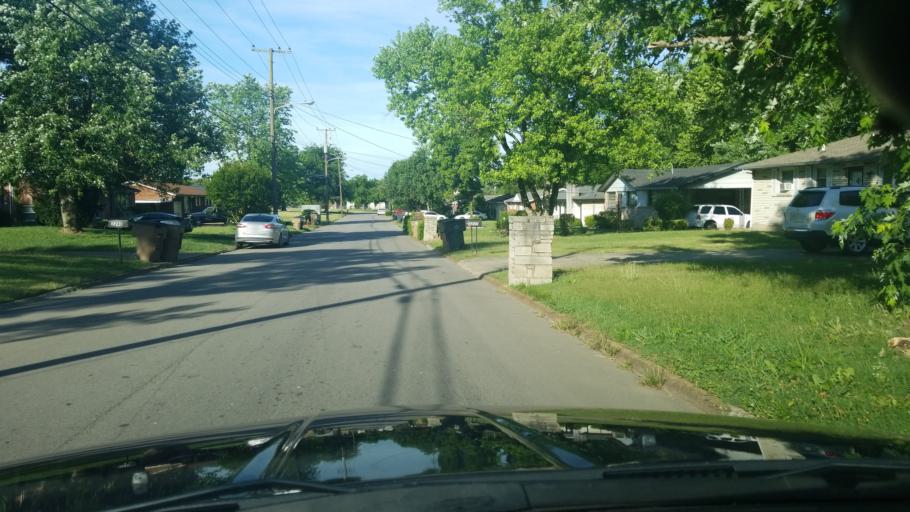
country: US
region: Tennessee
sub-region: Davidson County
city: Nashville
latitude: 36.2369
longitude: -86.7708
